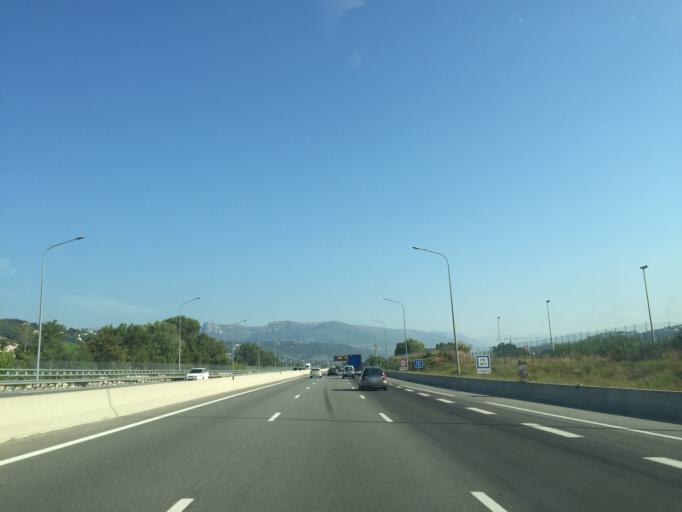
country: FR
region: Provence-Alpes-Cote d'Azur
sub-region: Departement des Alpes-Maritimes
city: Saint-Laurent-du-Var
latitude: 43.6789
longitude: 7.1941
